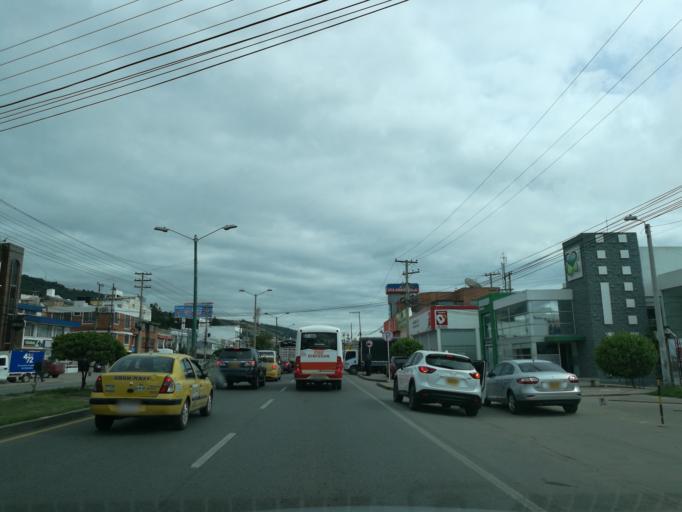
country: CO
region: Boyaca
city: Tunja
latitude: 5.5548
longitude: -73.3511
